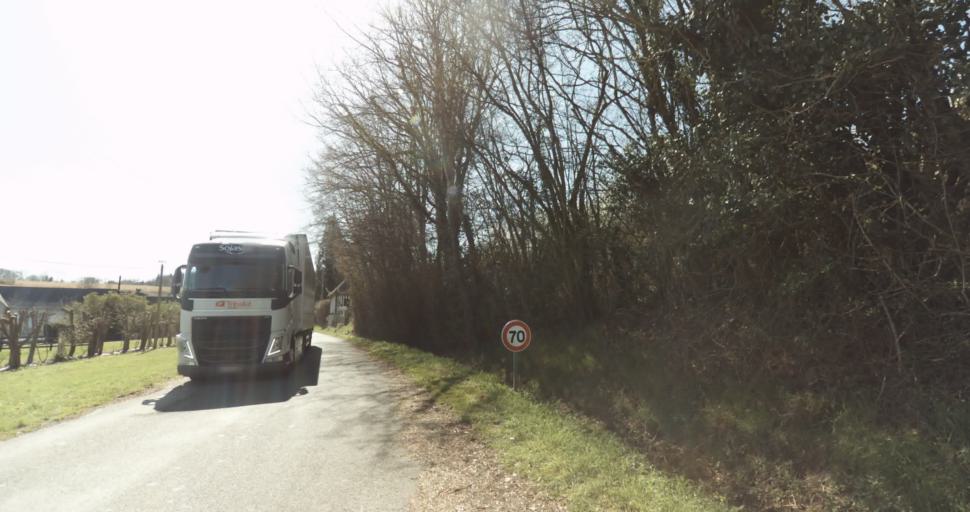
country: FR
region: Lower Normandy
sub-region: Departement du Calvados
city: Saint-Pierre-sur-Dives
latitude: 49.0137
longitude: 0.0573
